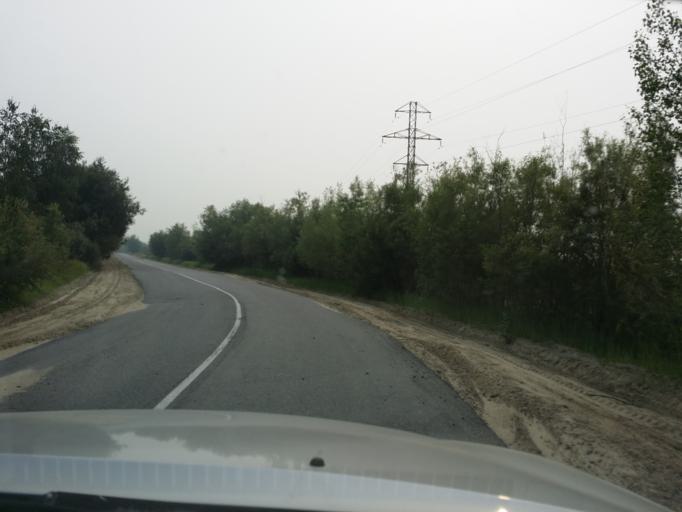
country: RU
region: Khanty-Mansiyskiy Avtonomnyy Okrug
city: Megion
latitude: 60.9975
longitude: 76.3019
